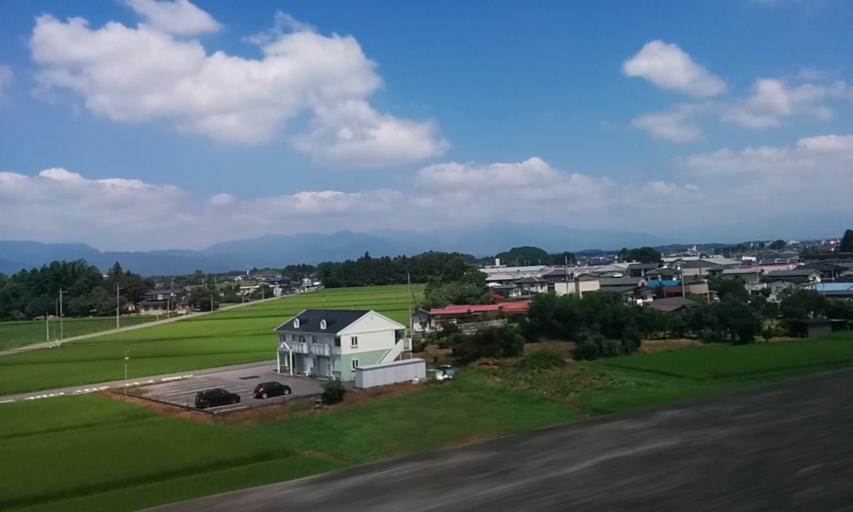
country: JP
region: Tochigi
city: Otawara
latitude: 36.8717
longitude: 139.9775
